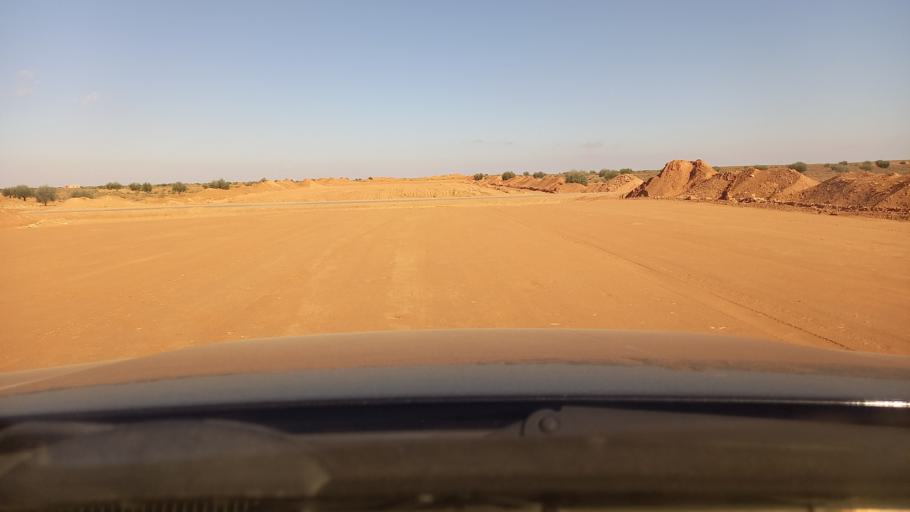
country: TN
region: Madanin
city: Medenine
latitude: 33.1773
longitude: 10.5289
